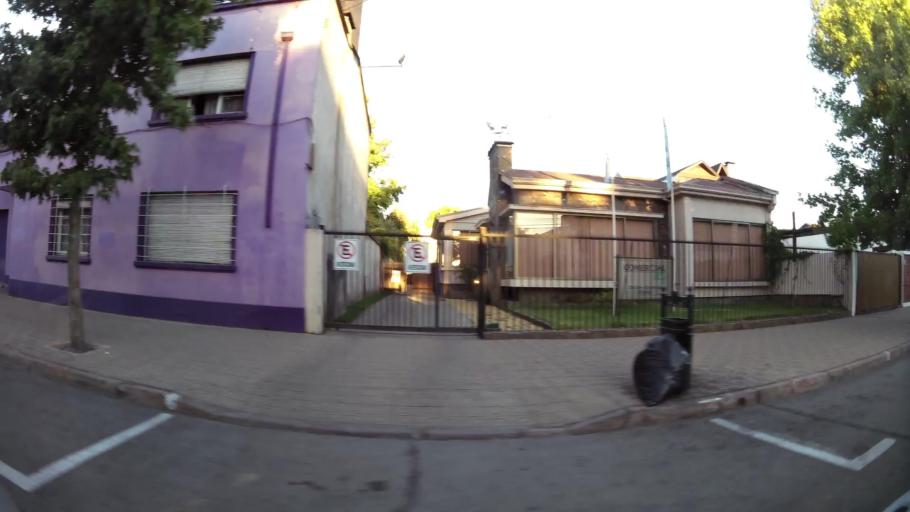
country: CL
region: Maule
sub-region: Provincia de Curico
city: Curico
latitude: -34.9863
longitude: -71.2385
